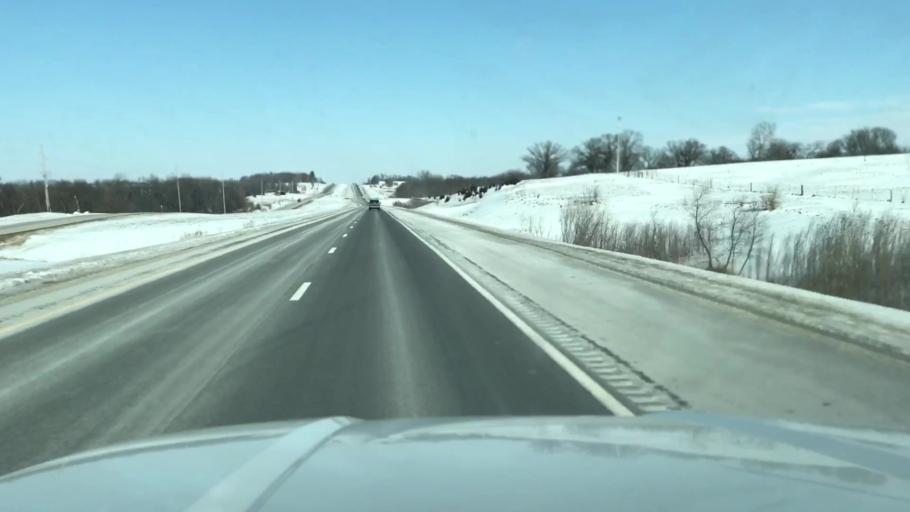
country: US
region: Missouri
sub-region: Nodaway County
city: Maryville
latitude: 40.1932
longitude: -94.8677
